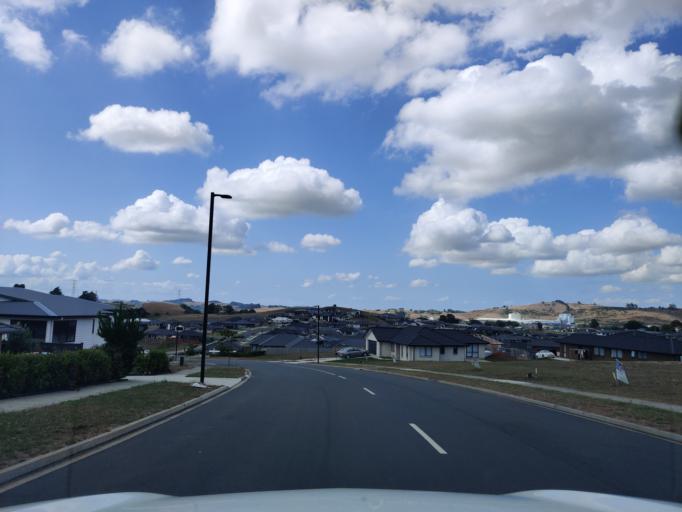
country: NZ
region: Auckland
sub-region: Auckland
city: Pukekohe East
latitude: -37.2346
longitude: 175.0149
